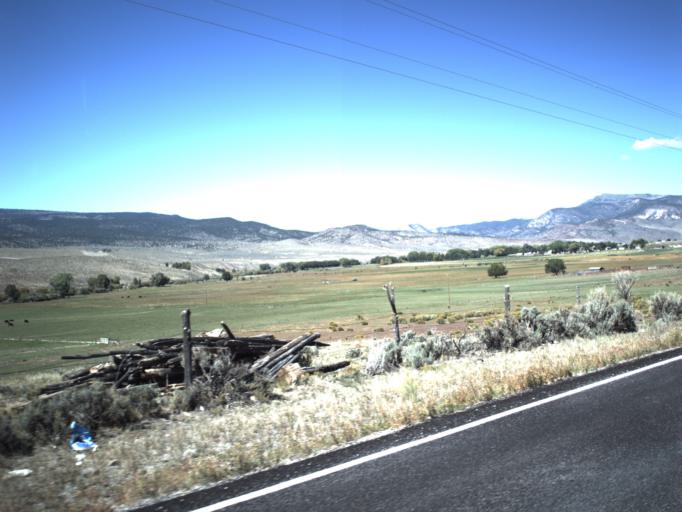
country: US
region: Utah
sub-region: Piute County
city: Junction
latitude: 38.0975
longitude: -111.9839
